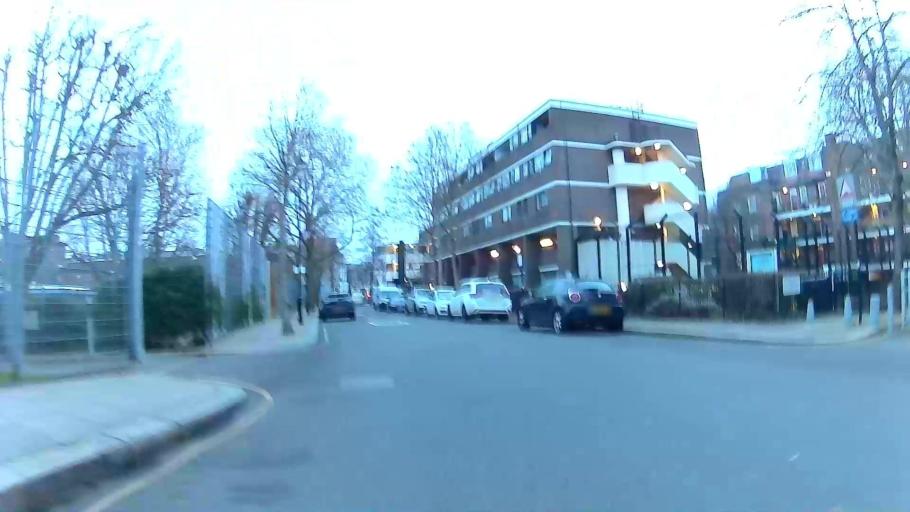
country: GB
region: England
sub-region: Greater London
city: Kensington
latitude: 51.5157
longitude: -0.2120
